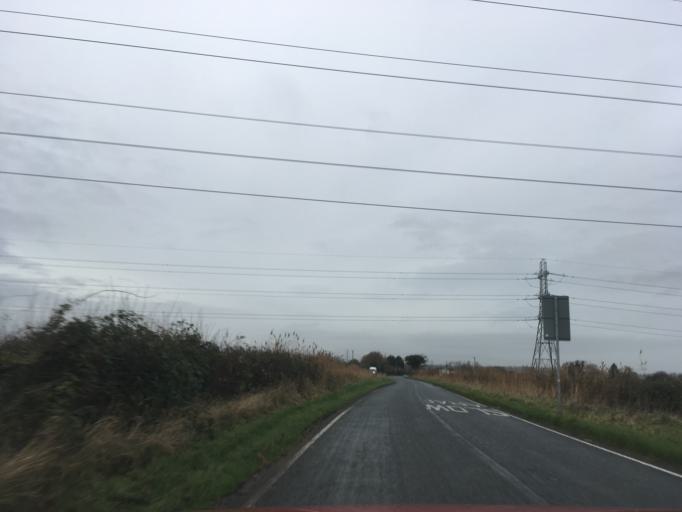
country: GB
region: Wales
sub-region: Newport
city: Nash
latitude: 51.5476
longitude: -2.9389
